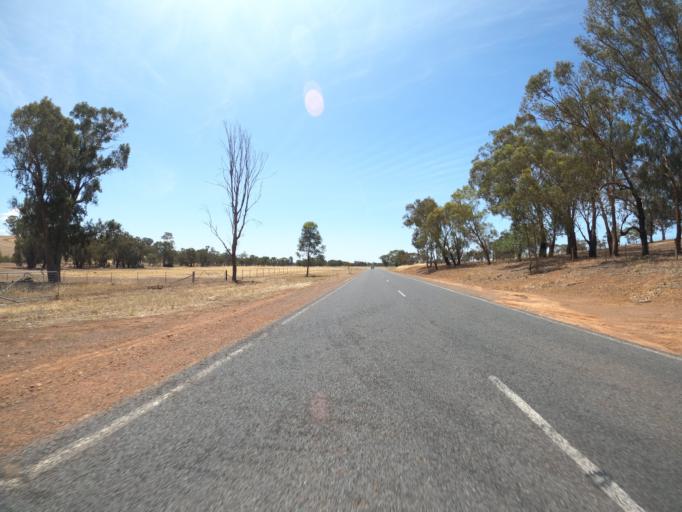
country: AU
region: Victoria
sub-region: Benalla
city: Benalla
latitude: -36.3328
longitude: 145.9604
